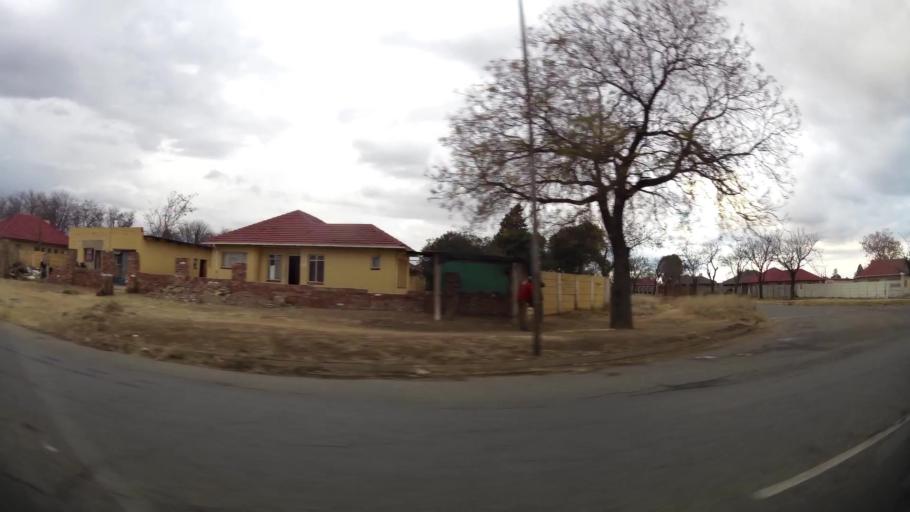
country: ZA
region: Orange Free State
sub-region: Lejweleputswa District Municipality
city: Welkom
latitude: -27.9578
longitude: 26.7197
